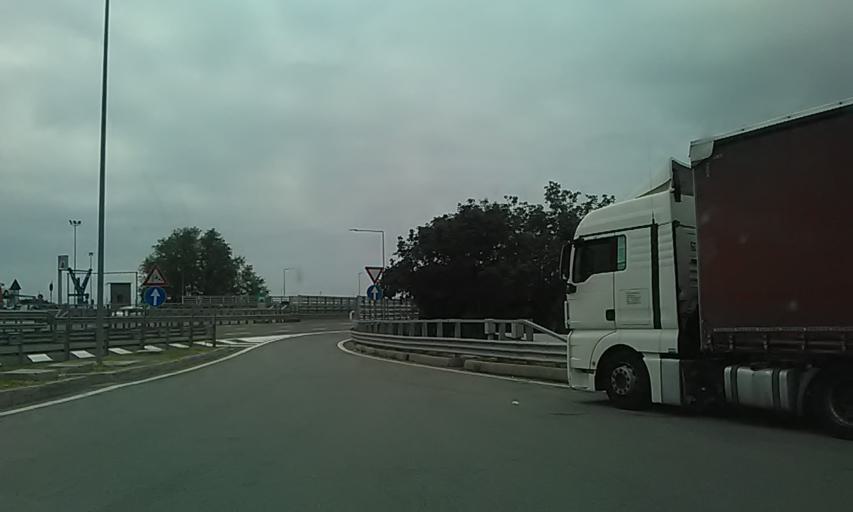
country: IT
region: Liguria
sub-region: Provincia di Genova
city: Mele
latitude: 44.4545
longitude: 8.7442
